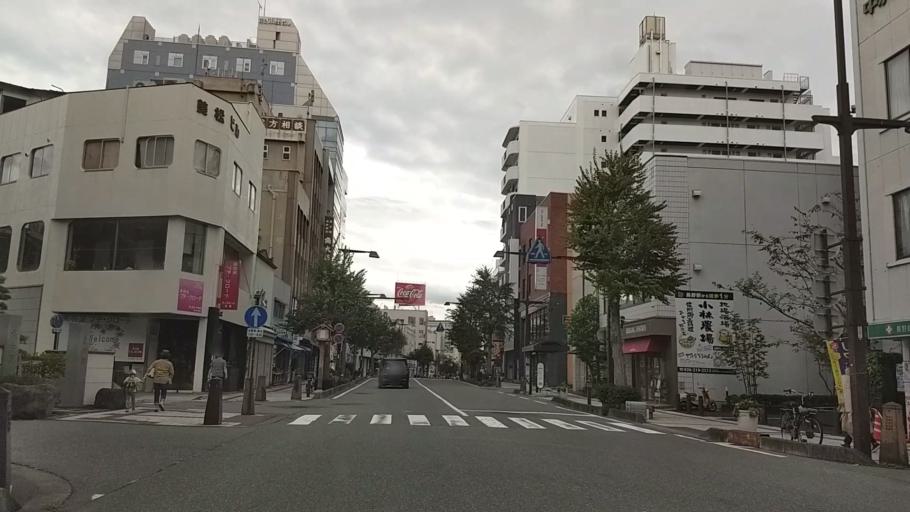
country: JP
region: Nagano
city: Nagano-shi
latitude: 36.6486
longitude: 138.1872
